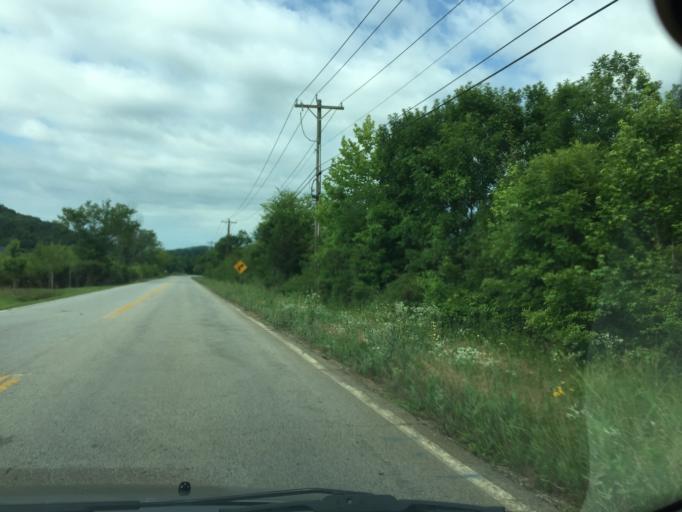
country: US
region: Tennessee
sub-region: Hamilton County
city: Apison
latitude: 34.9909
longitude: -85.0612
